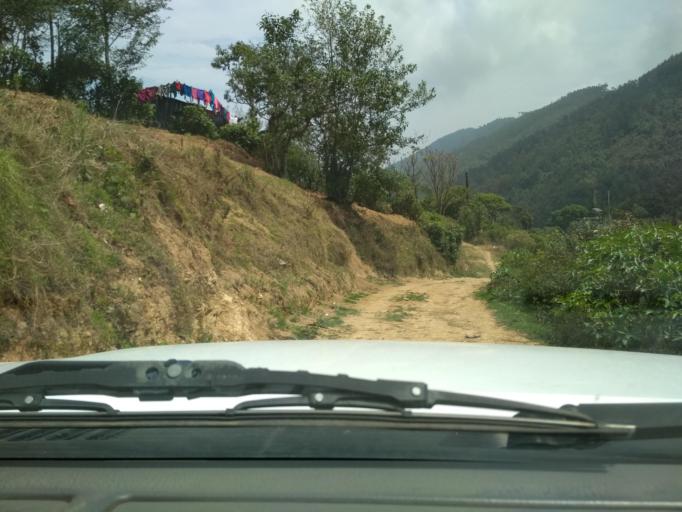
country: MX
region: Veracruz
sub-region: Camerino Z. Mendoza
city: Necoxtla
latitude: 18.7820
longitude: -97.1546
